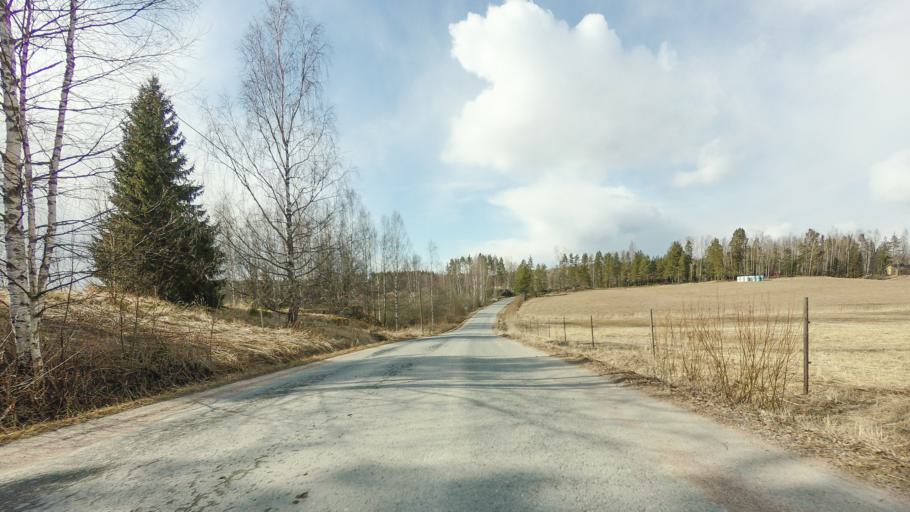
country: FI
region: Varsinais-Suomi
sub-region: Salo
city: Suomusjaervi
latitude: 60.3170
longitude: 23.7098
